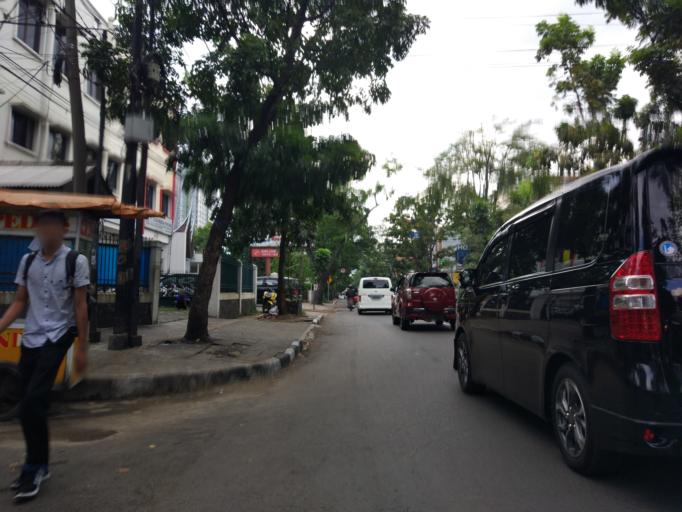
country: ID
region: West Java
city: Bandung
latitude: -6.9230
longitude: 107.6220
